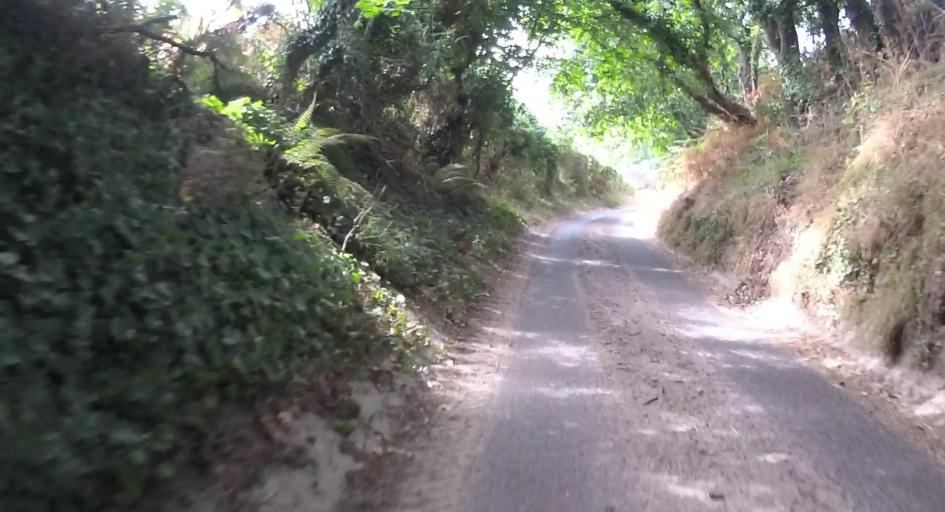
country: GB
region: England
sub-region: Dorset
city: Wareham
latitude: 50.6380
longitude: -2.0508
